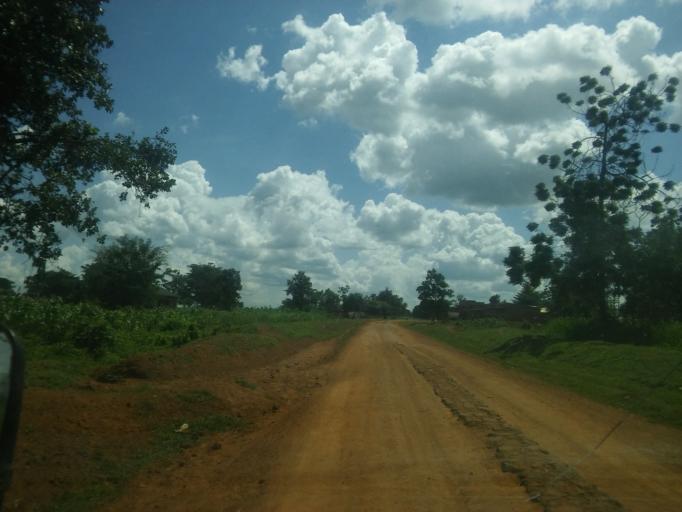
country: UG
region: Eastern Region
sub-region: Pallisa District
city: Pallisa
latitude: 1.1515
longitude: 33.8082
